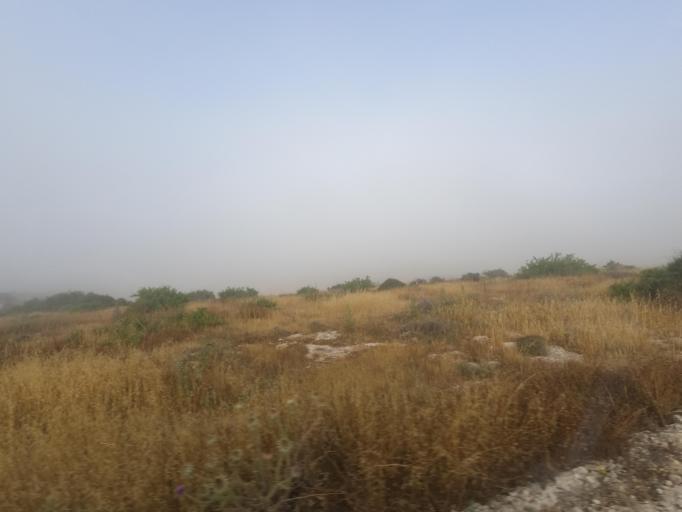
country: CY
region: Ammochostos
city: Acheritou
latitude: 35.0987
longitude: 33.8775
